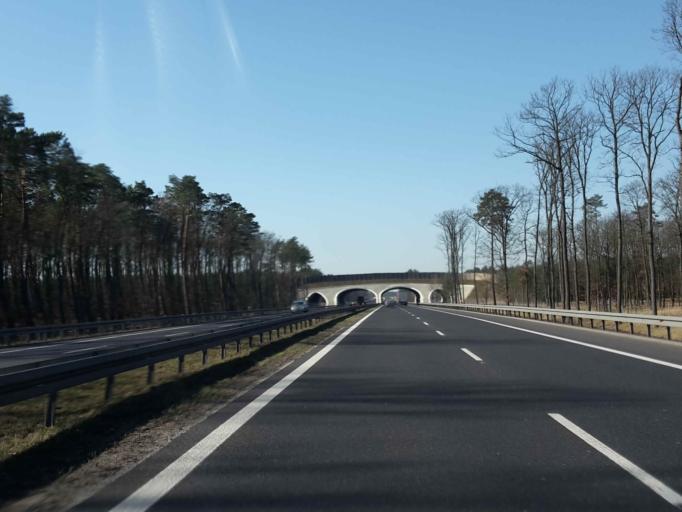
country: PL
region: Greater Poland Voivodeship
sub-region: Powiat poznanski
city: Pobiedziska
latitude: 52.4495
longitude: 17.3697
